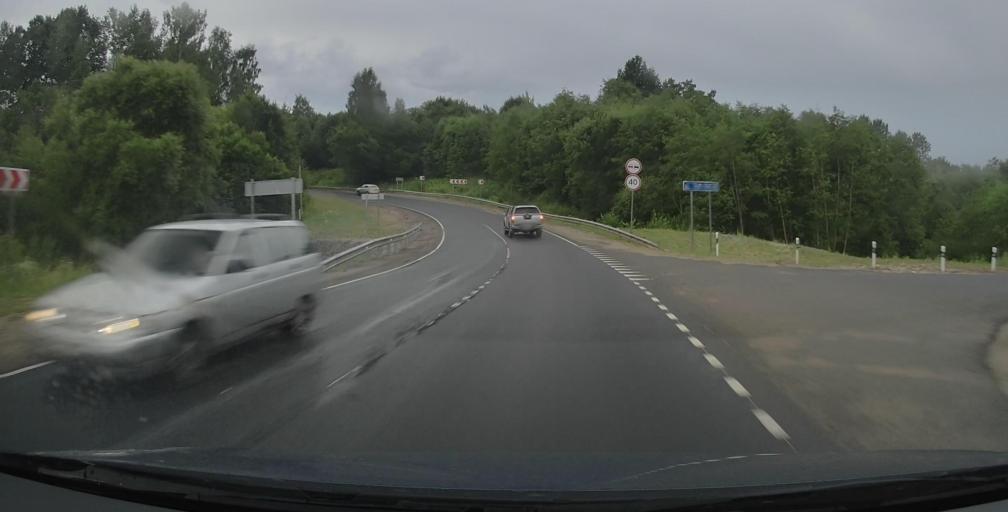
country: RU
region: Jaroslavl
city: Uglich
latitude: 57.5576
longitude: 38.2762
